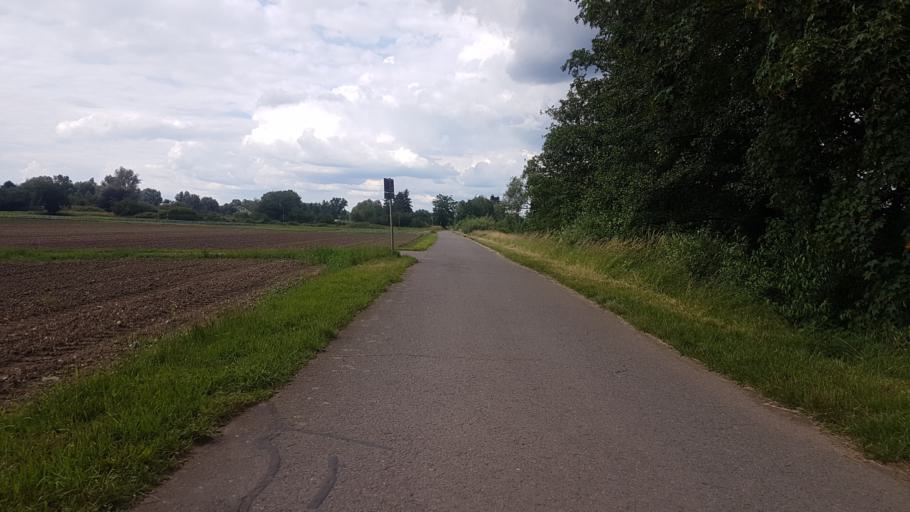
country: DE
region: Saarland
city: Ensdorf
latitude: 49.2905
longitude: 6.7646
